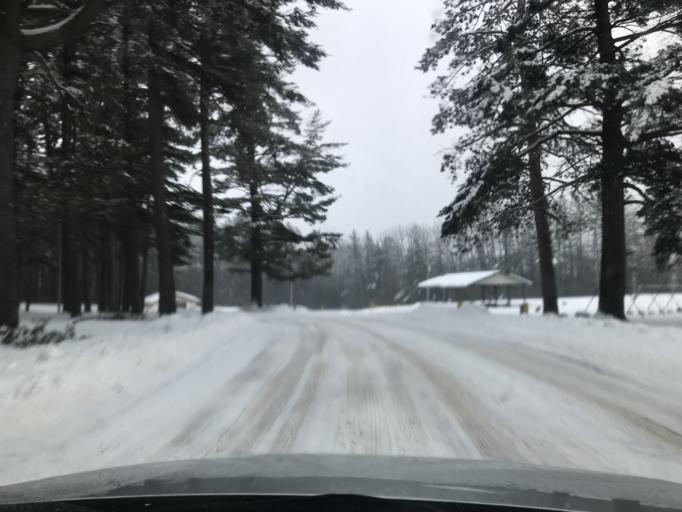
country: US
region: Wisconsin
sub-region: Marinette County
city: Peshtigo
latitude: 45.3808
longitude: -87.9518
